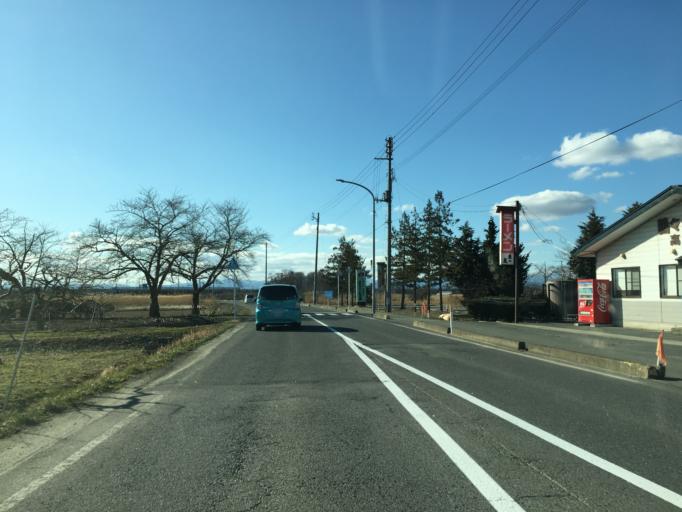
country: JP
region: Yamagata
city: Takahata
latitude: 38.0044
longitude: 140.1625
